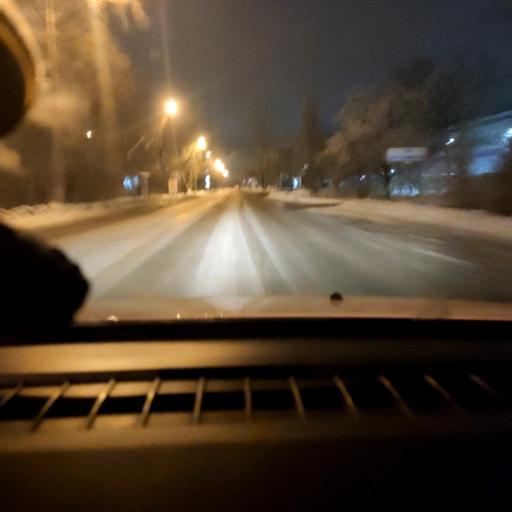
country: RU
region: Samara
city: Samara
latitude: 53.1081
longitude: 50.0708
